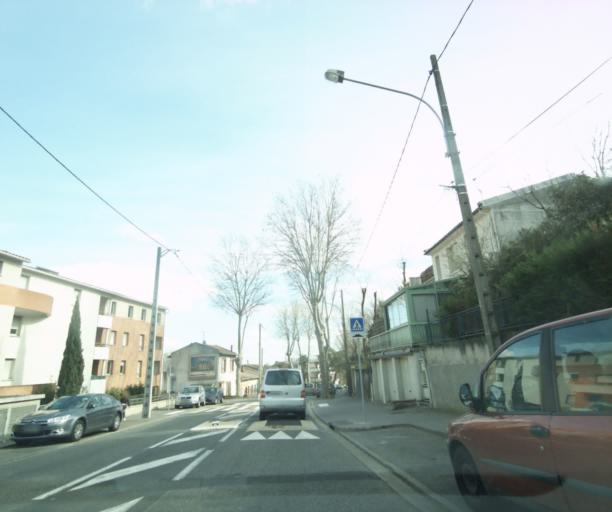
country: FR
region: Midi-Pyrenees
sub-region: Departement de la Haute-Garonne
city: Balma
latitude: 43.5985
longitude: 1.4805
